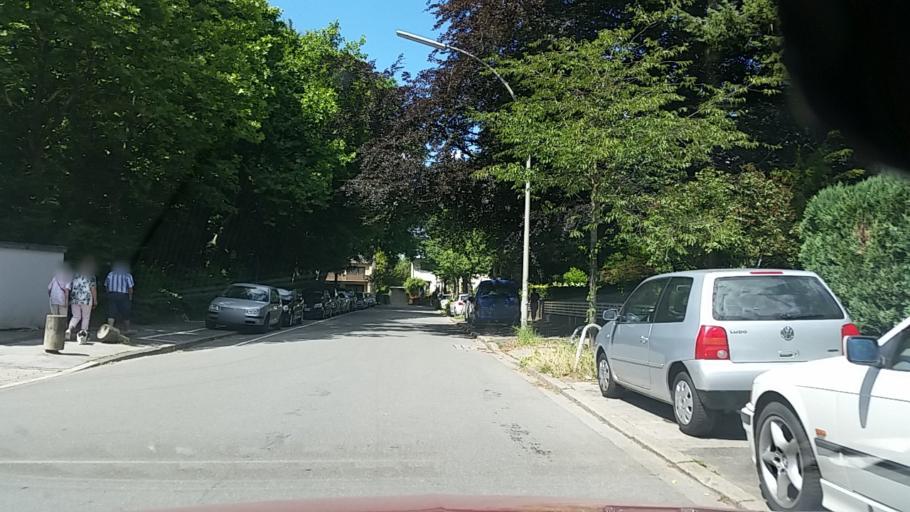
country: DE
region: Hamburg
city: Marienthal
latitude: 53.5703
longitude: 10.0906
